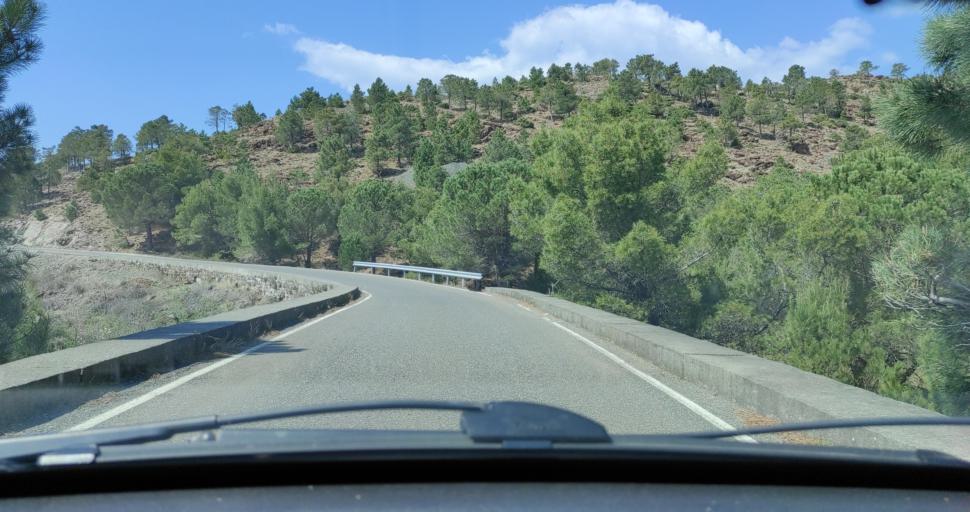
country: AL
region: Shkoder
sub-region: Rrethi i Shkodres
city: Hajmel
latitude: 41.9820
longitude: 19.6465
